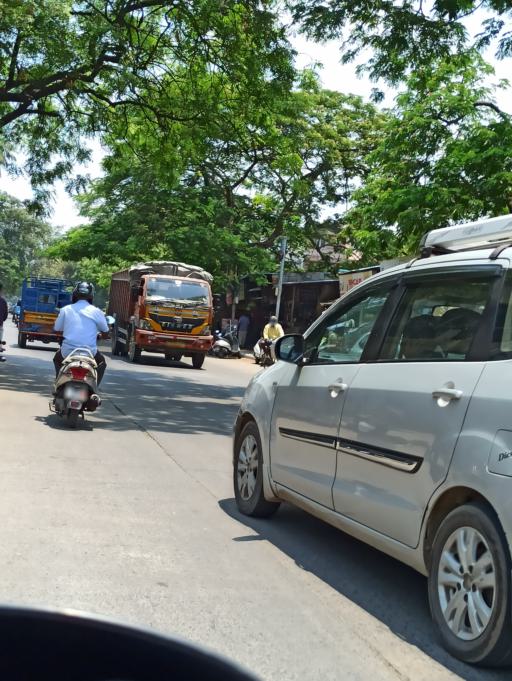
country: IN
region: Tamil Nadu
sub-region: Chennai
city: Chetput
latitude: 13.0864
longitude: 80.2346
